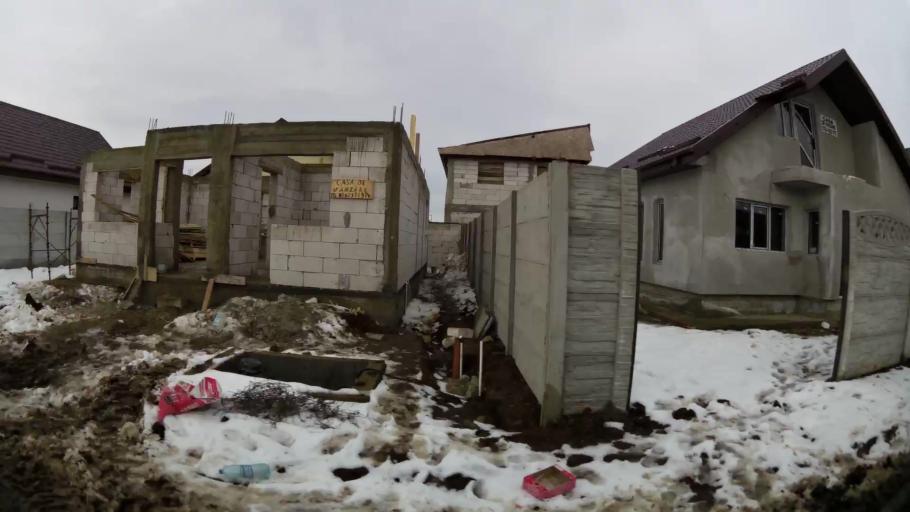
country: RO
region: Ilfov
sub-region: Comuna Pantelimon
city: Pantelimon
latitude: 44.4582
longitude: 26.1962
